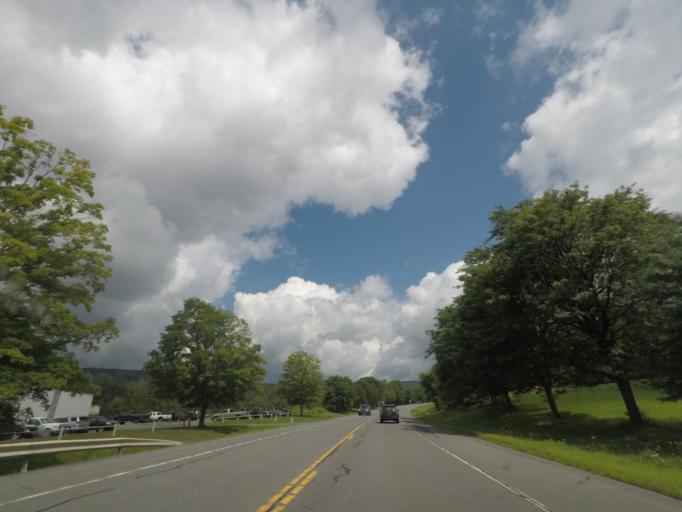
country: US
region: Massachusetts
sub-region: Berkshire County
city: Lanesborough
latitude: 42.6113
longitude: -73.3761
